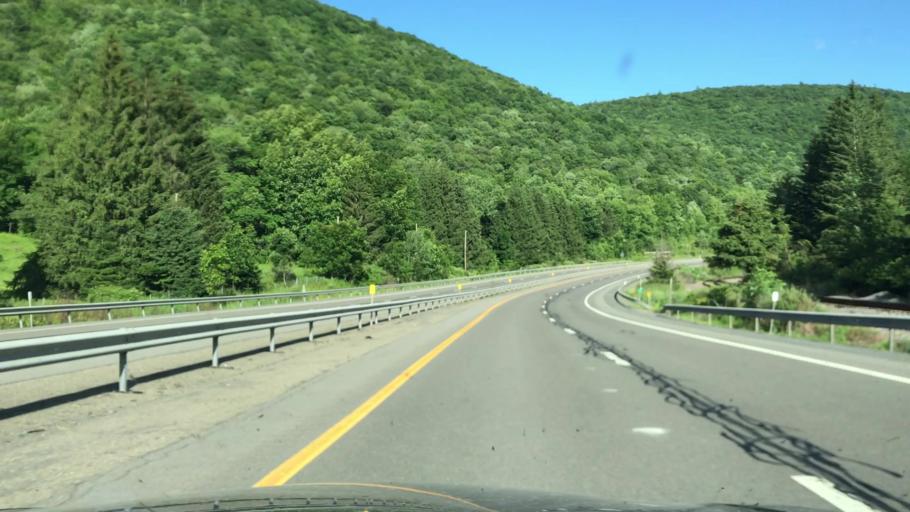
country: US
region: New York
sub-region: Delaware County
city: Hancock
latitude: 41.9961
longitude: -75.3442
